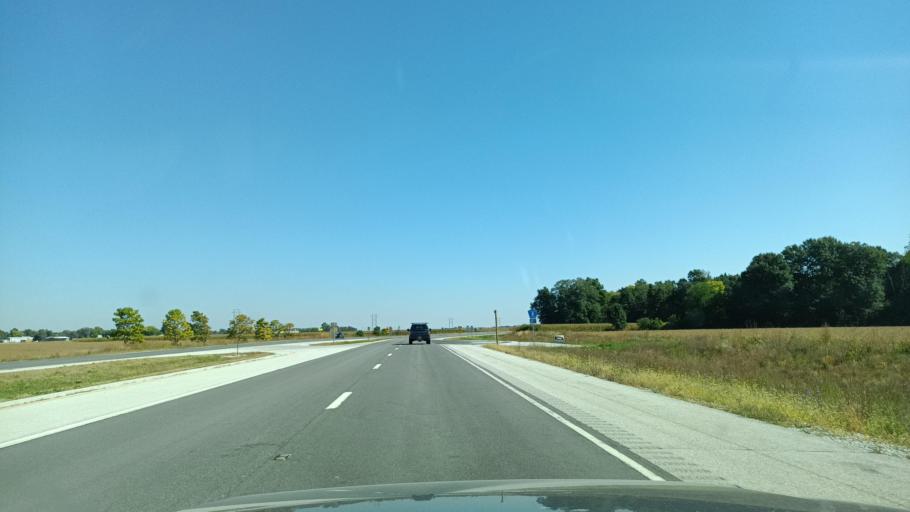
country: US
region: Illinois
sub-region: McDonough County
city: Colchester
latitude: 40.4093
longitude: -90.7970
